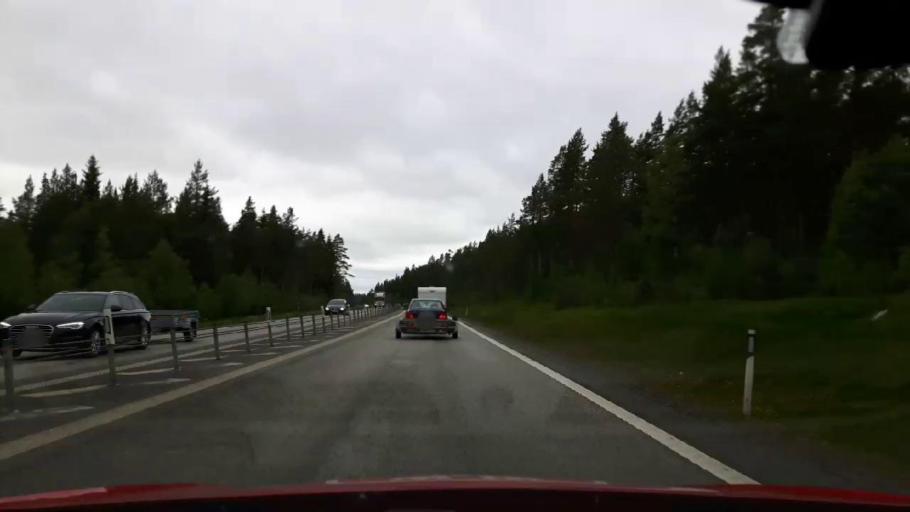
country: SE
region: Jaemtland
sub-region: OEstersunds Kommun
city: Ostersund
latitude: 63.1972
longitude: 14.6859
